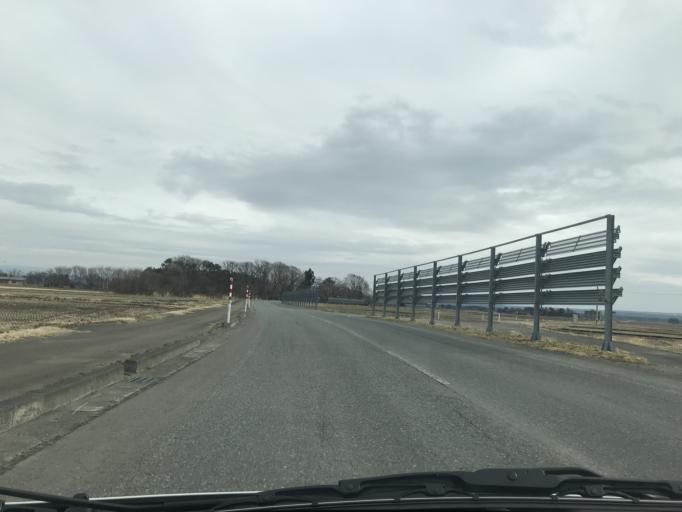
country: JP
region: Iwate
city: Hanamaki
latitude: 39.3463
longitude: 140.9852
